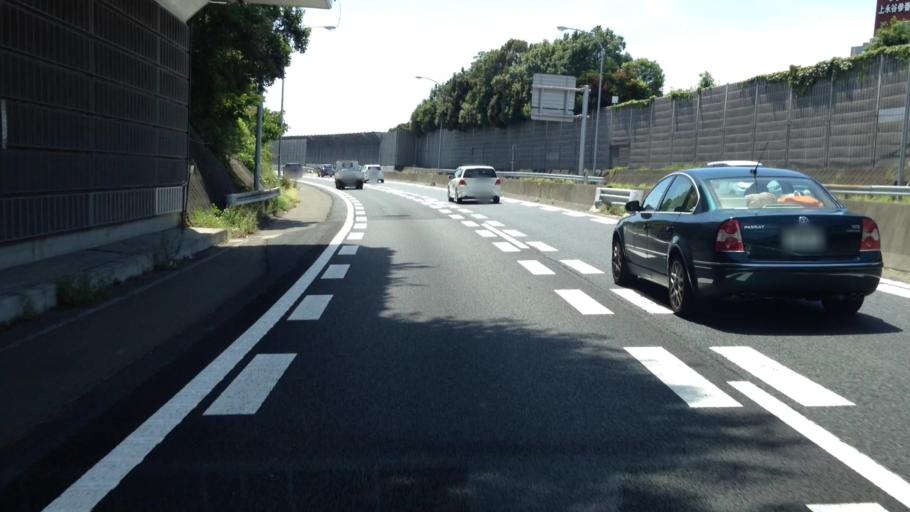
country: JP
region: Kanagawa
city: Yokohama
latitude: 35.4102
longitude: 139.5754
